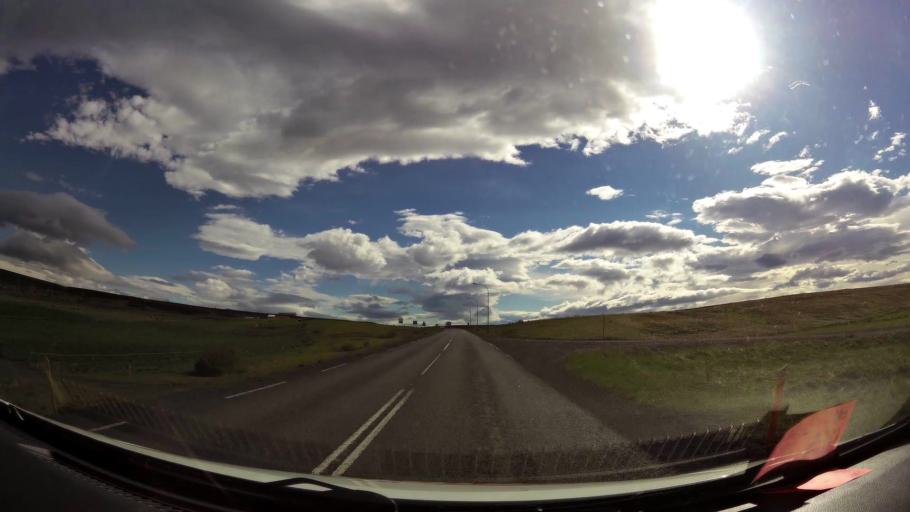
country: IS
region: Northwest
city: Saudarkrokur
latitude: 65.6551
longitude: -20.2859
